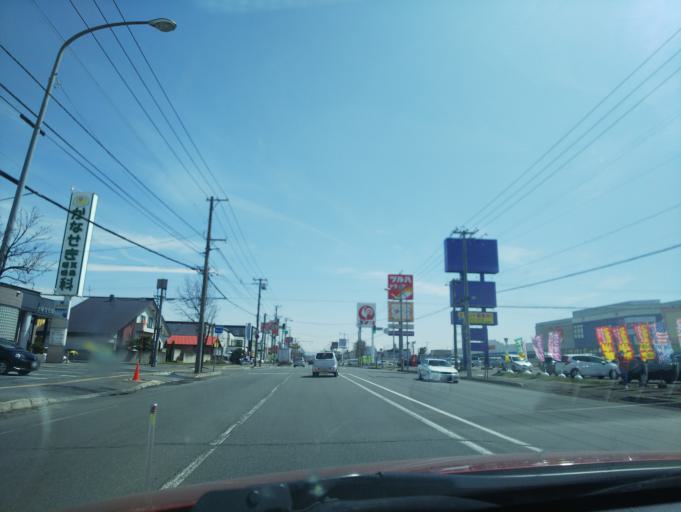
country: JP
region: Hokkaido
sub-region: Asahikawa-shi
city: Asahikawa
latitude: 43.7866
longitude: 142.4096
